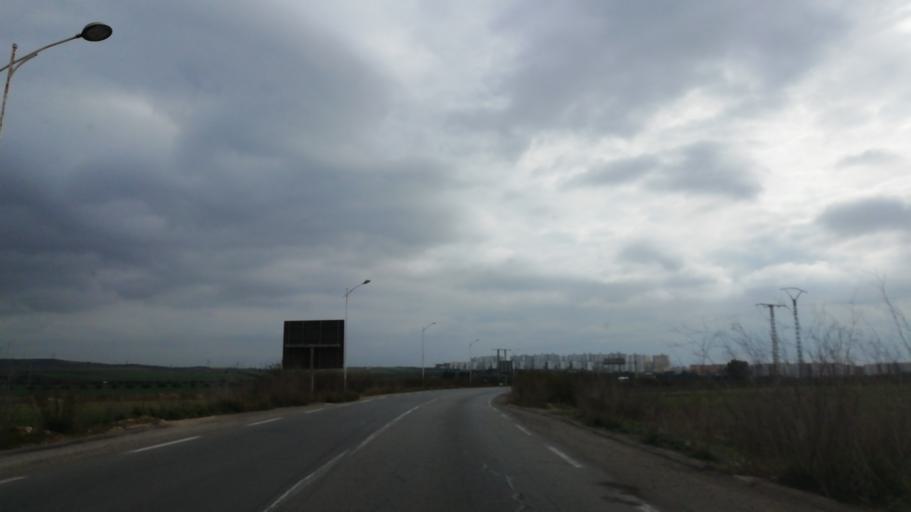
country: DZ
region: Oran
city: Sidi ech Chahmi
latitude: 35.5664
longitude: -0.4483
